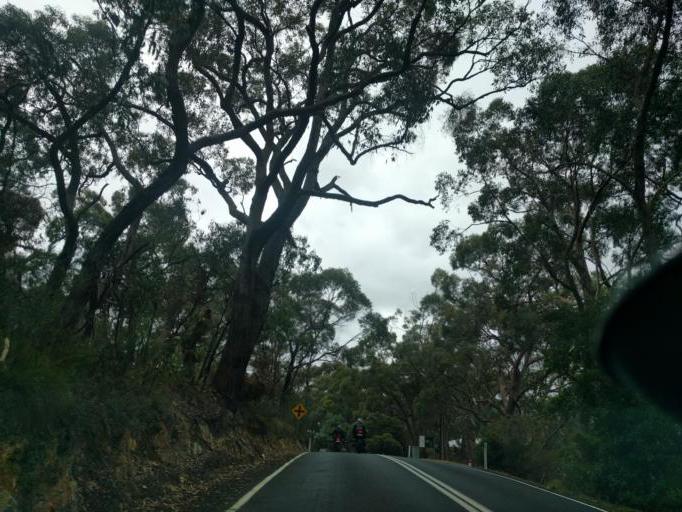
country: AU
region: South Australia
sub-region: Adelaide Hills
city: Stirling
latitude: -35.0250
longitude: 138.7549
